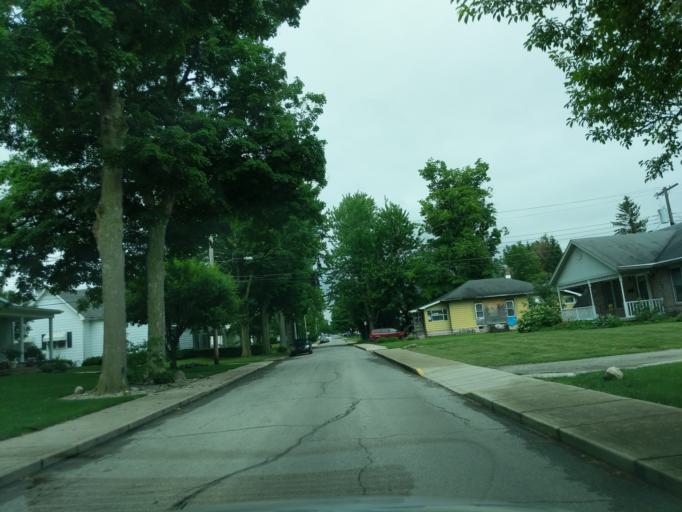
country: US
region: Indiana
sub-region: Tipton County
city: Tipton
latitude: 40.2795
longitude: -86.0441
